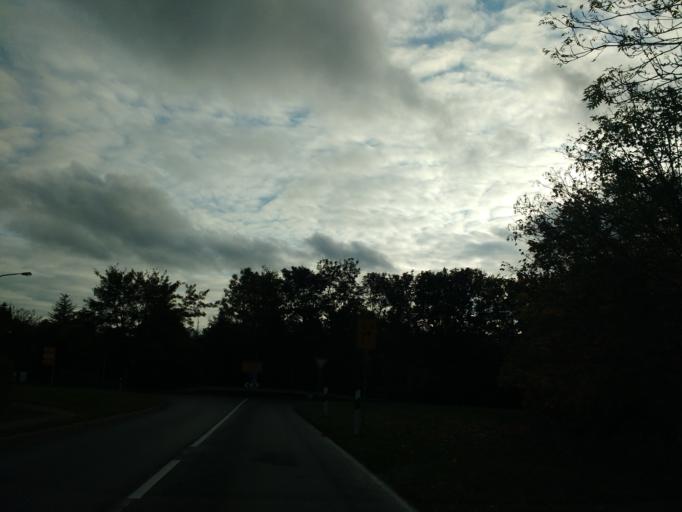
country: DE
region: Schleswig-Holstein
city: Schonwalde am Bungsberg
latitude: 54.1909
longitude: 10.7537
